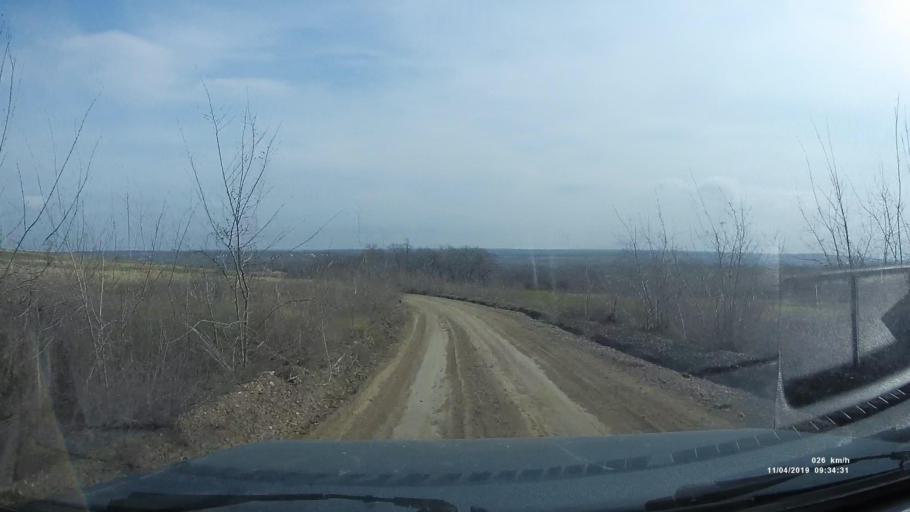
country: RU
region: Rostov
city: Staraya Stanitsa
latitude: 48.2692
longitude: 40.3702
